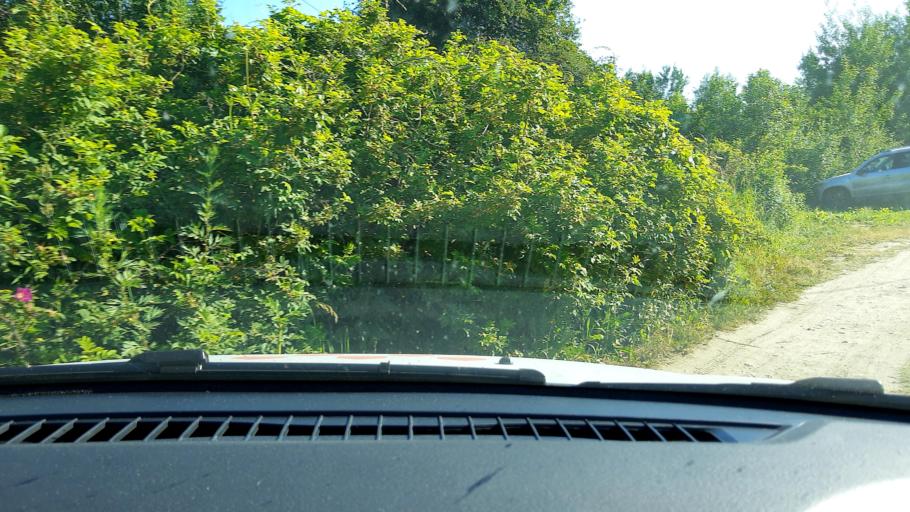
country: RU
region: Nizjnij Novgorod
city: Neklyudovo
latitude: 56.4306
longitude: 44.0090
